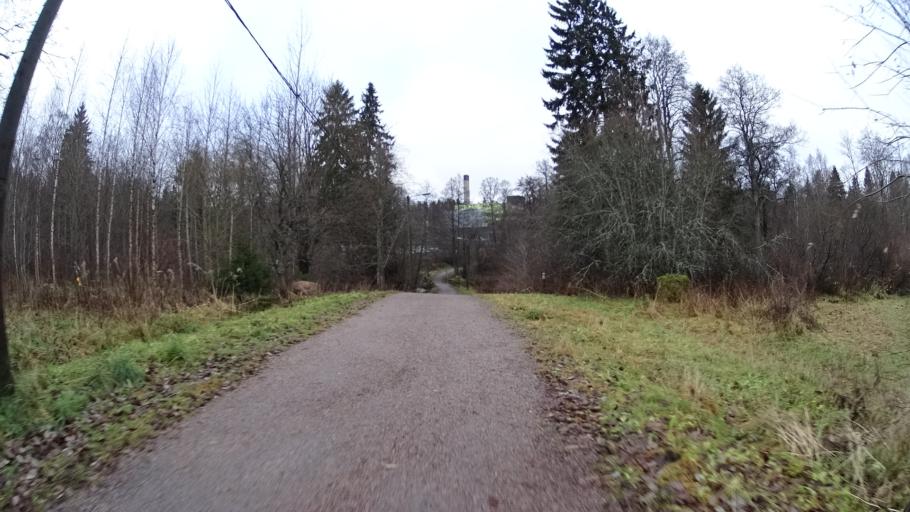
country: FI
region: Uusimaa
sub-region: Helsinki
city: Espoo
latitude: 60.2250
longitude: 24.6880
